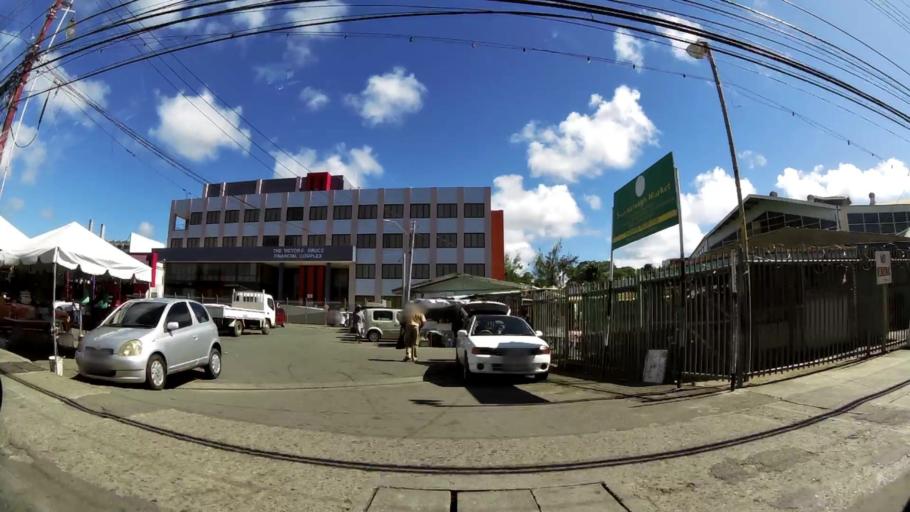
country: TT
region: Tobago
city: Scarborough
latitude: 11.1840
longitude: -60.7377
